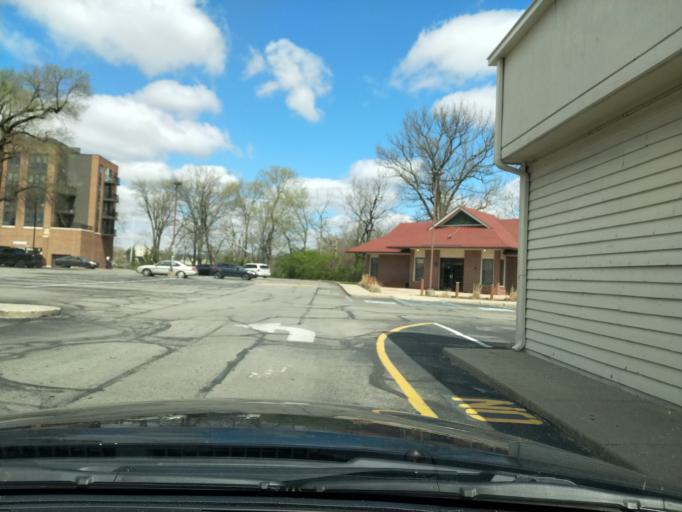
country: US
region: Indiana
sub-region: Marion County
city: Broad Ripple
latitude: 39.8701
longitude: -86.1401
